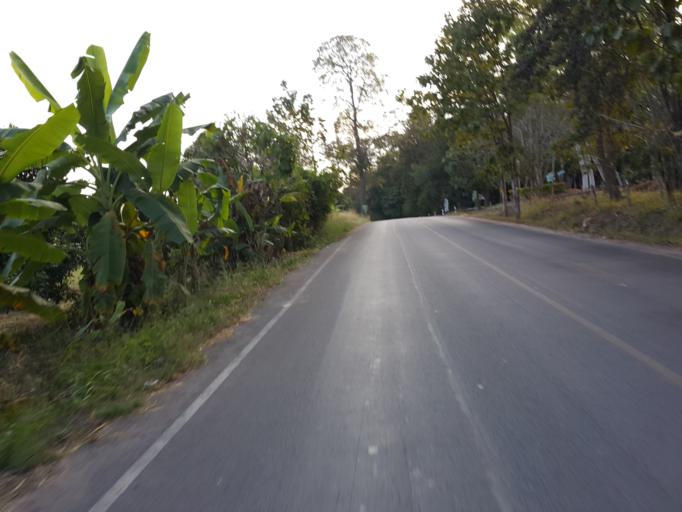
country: TH
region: Lamphun
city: Thung Hua Chang
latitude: 18.0356
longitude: 99.0298
